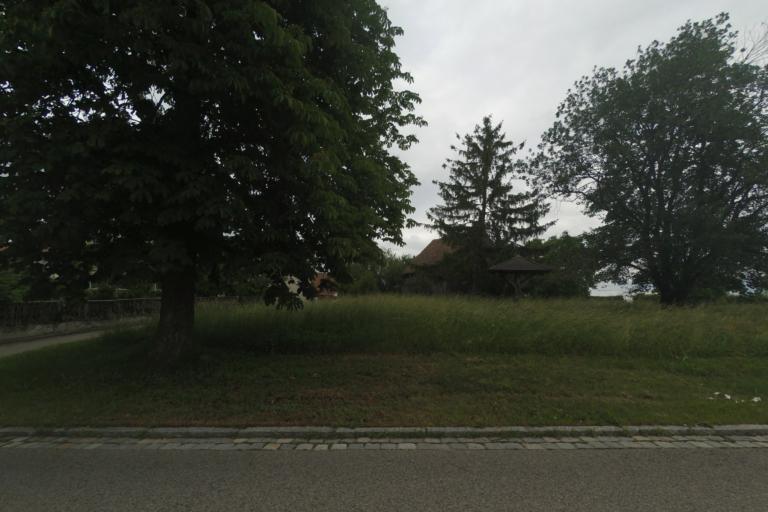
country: DE
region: Bavaria
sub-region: Regierungsbezirk Mittelfranken
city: Simmershofen
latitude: 49.5345
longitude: 10.1622
